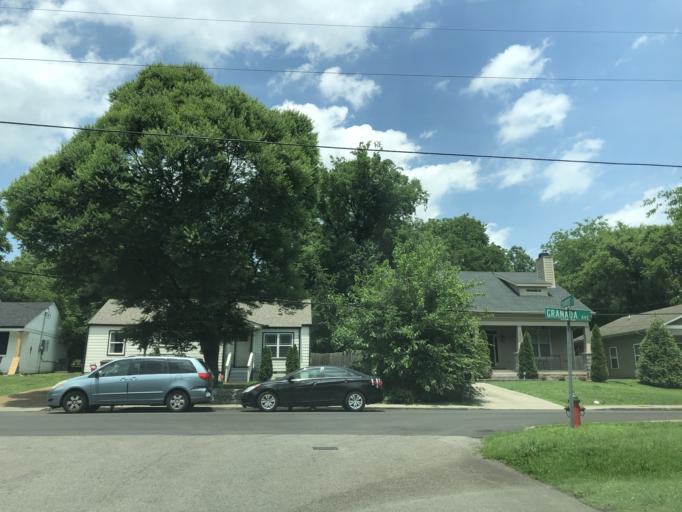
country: US
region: Tennessee
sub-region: Davidson County
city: Nashville
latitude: 36.1885
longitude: -86.7499
